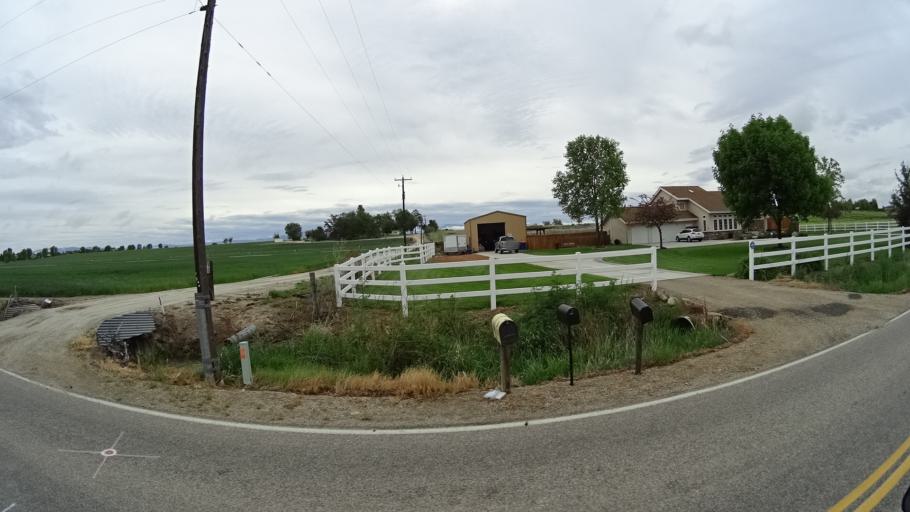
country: US
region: Idaho
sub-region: Ada County
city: Star
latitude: 43.7137
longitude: -116.4685
